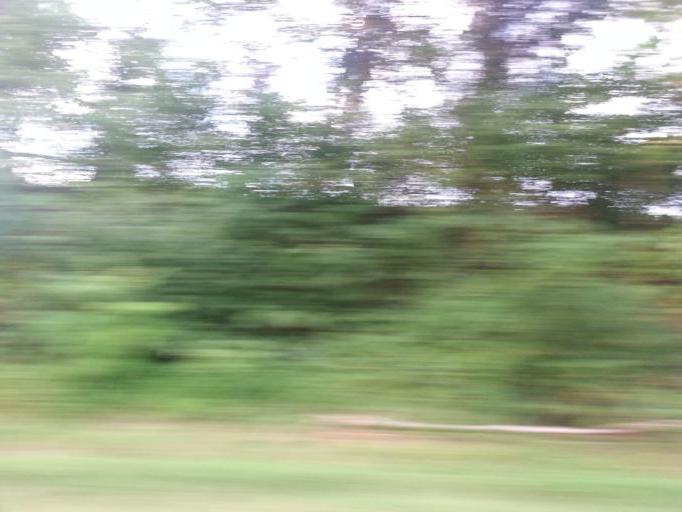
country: US
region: Tennessee
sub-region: Blount County
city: Alcoa
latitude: 35.8051
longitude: -83.9619
